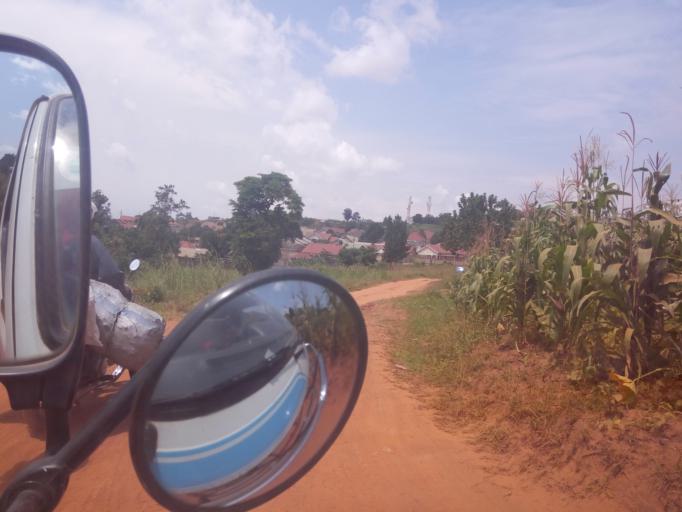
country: UG
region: Central Region
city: Kampala Central Division
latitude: 0.3855
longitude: 32.5482
